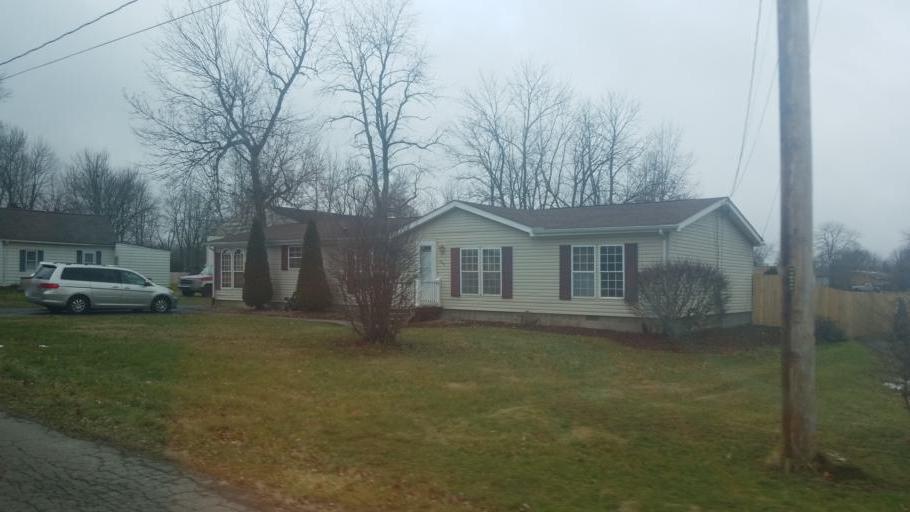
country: US
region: Ohio
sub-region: Crawford County
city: Galion
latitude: 40.7284
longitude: -82.7711
